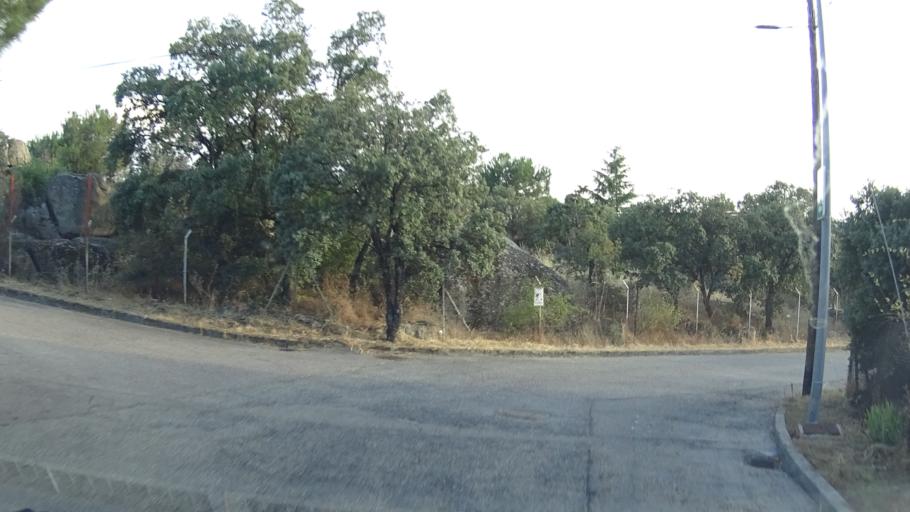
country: ES
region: Madrid
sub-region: Provincia de Madrid
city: Torrelodones
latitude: 40.5888
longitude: -3.9451
